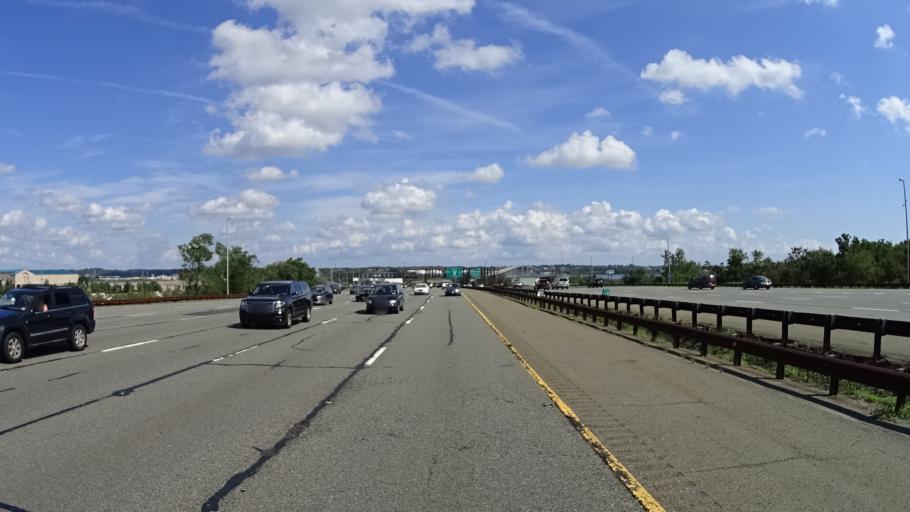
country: US
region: New Jersey
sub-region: Middlesex County
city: South Amboy
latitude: 40.4910
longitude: -74.3014
